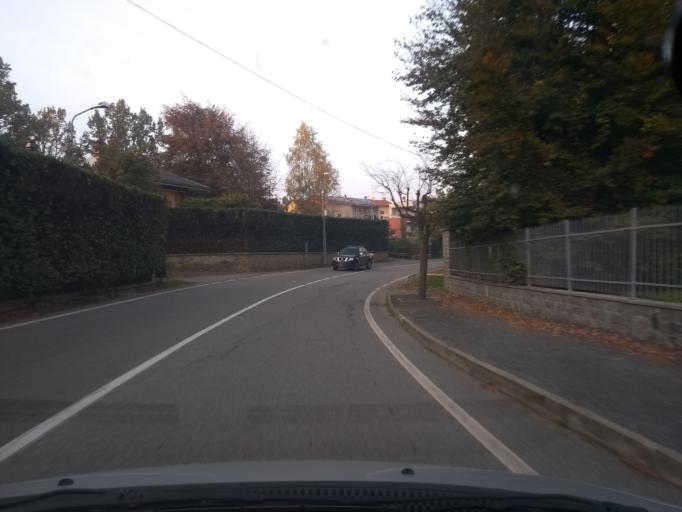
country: IT
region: Piedmont
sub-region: Provincia di Torino
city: La Cassa
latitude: 45.1789
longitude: 7.5151
